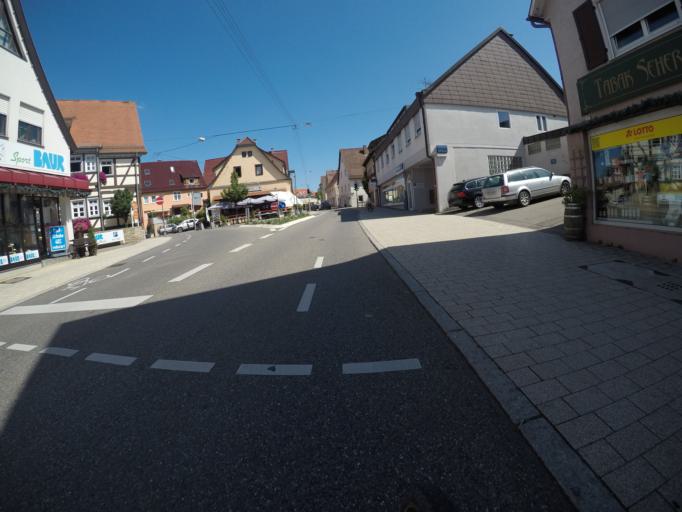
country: DE
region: Baden-Wuerttemberg
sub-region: Regierungsbezirk Stuttgart
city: Filderstadt
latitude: 48.7009
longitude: 9.2128
